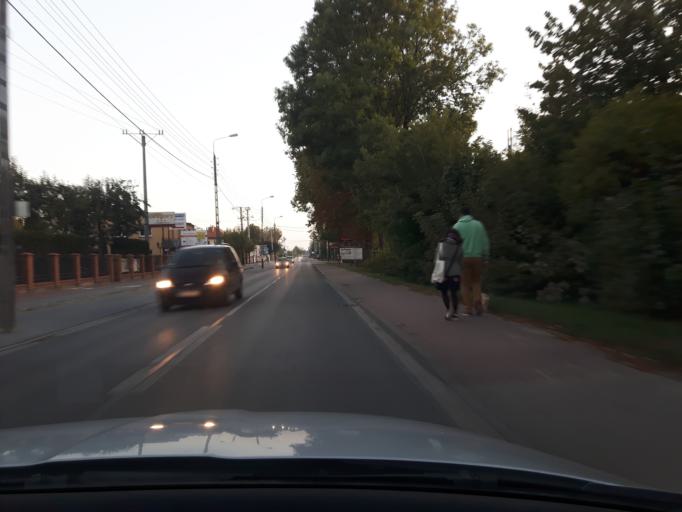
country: PL
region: Masovian Voivodeship
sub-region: Powiat wolominski
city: Kobylka
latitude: 52.3355
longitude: 21.1945
